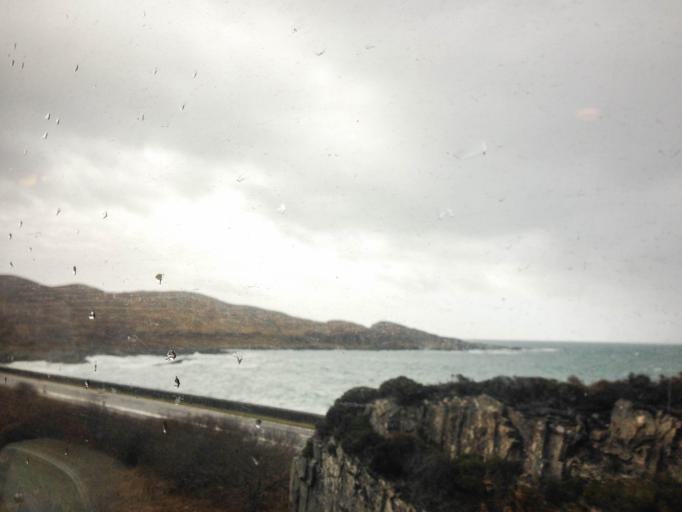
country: GB
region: Scotland
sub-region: Highland
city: Portree
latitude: 56.9973
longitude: -5.8321
